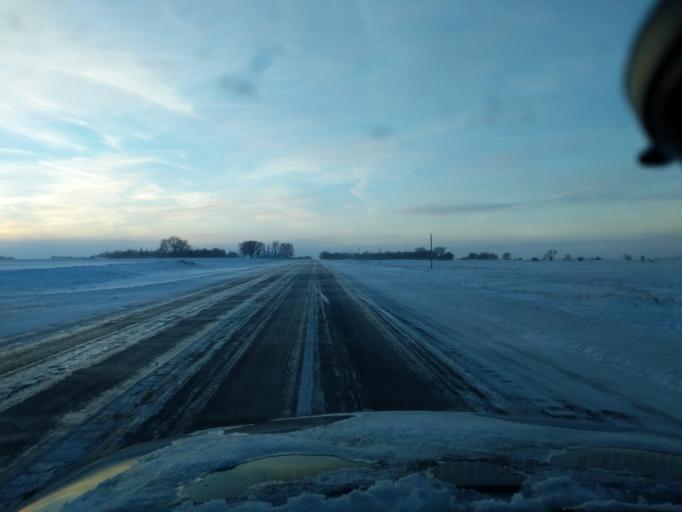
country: US
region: Minnesota
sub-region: Renville County
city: Renville
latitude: 44.7889
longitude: -95.2630
